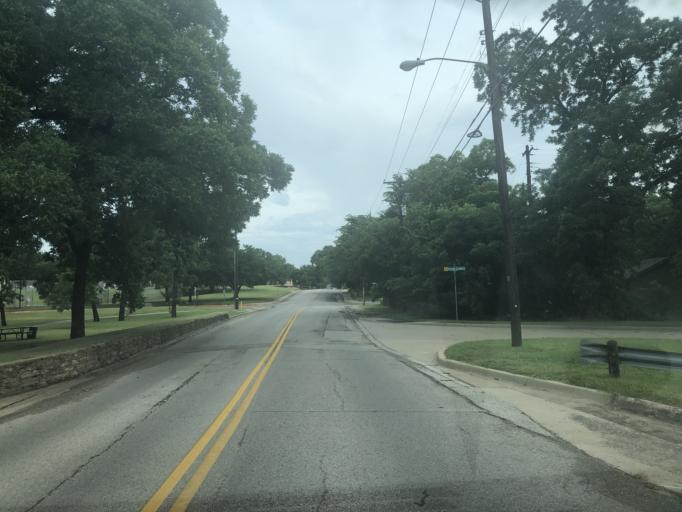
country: US
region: Texas
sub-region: Dallas County
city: Irving
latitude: 32.8033
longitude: -96.9469
